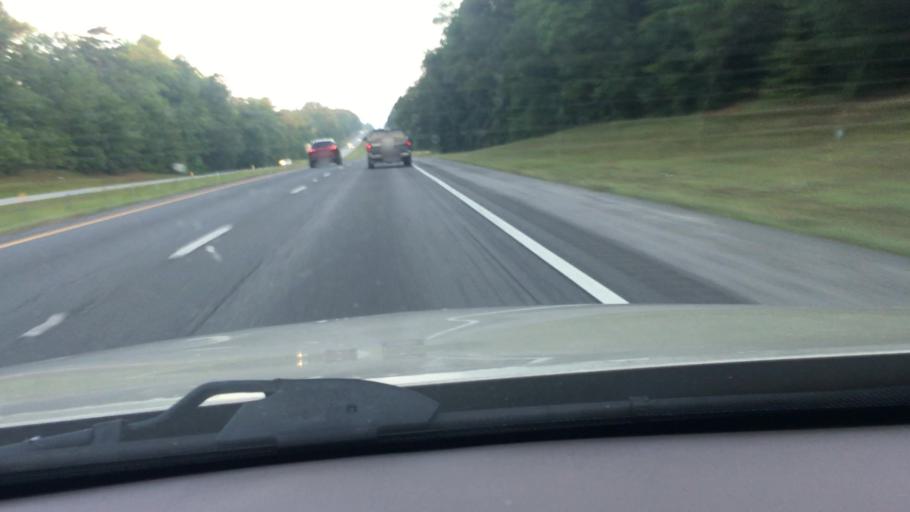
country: US
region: South Carolina
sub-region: Richland County
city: Lake Murray of Richland
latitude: 34.1514
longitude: -81.2507
